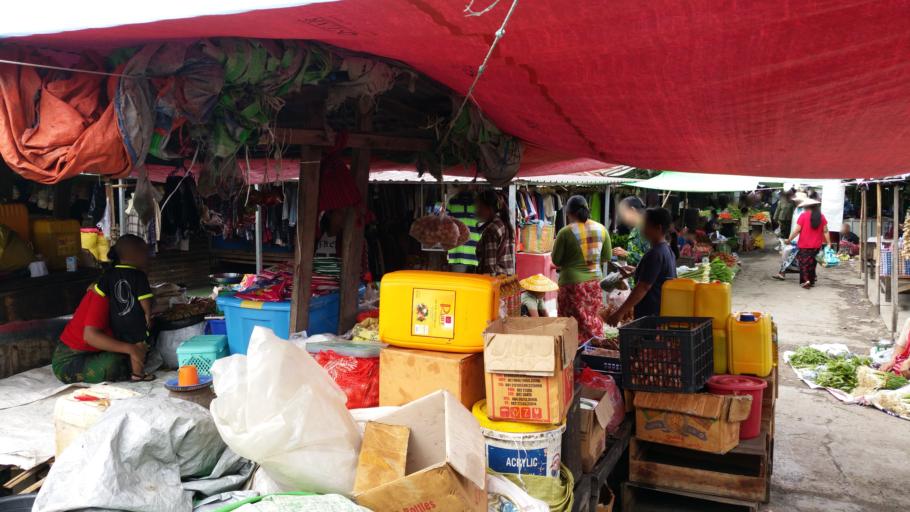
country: MM
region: Shan
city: Taunggyi
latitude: 20.6621
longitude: 96.9316
